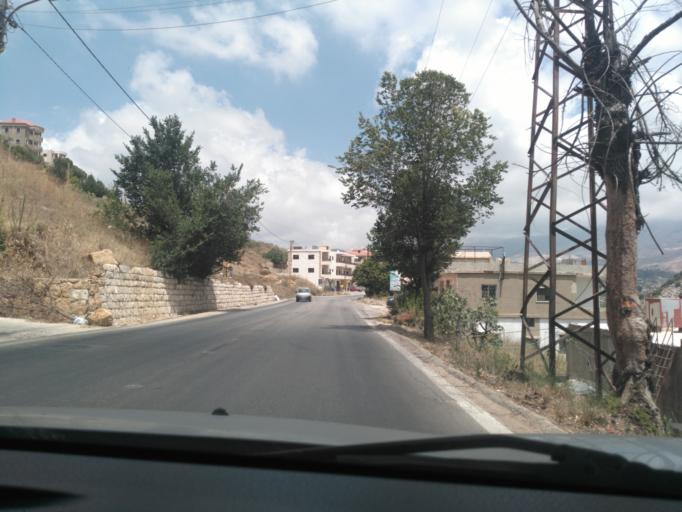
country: LB
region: Mont-Liban
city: Beit ed Dine
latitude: 33.6999
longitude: 35.6590
